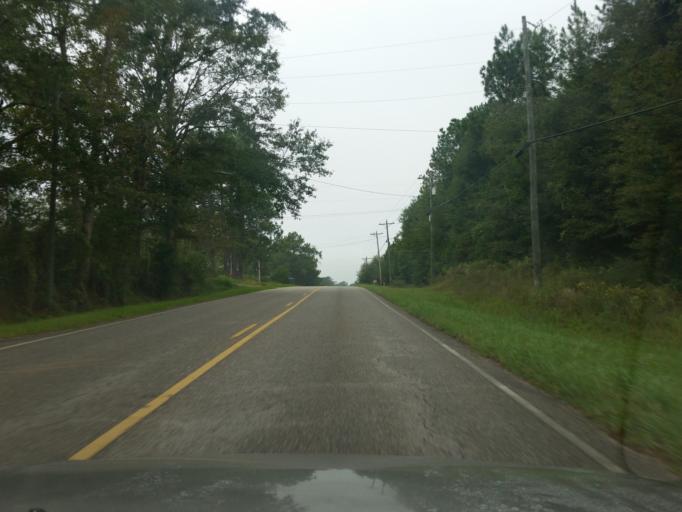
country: US
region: Alabama
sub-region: Baldwin County
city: Bay Minette
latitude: 30.8524
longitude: -87.8103
